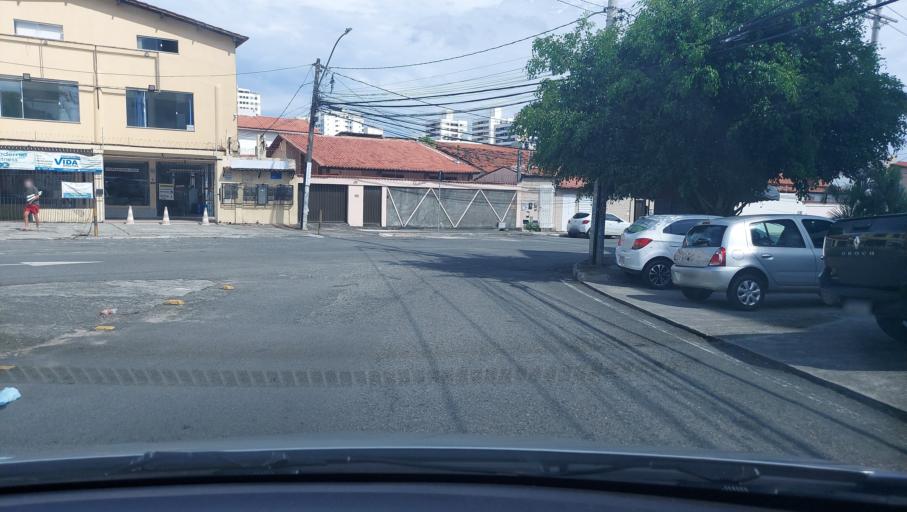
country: BR
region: Bahia
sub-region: Salvador
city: Salvador
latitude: -12.9811
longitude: -38.4459
